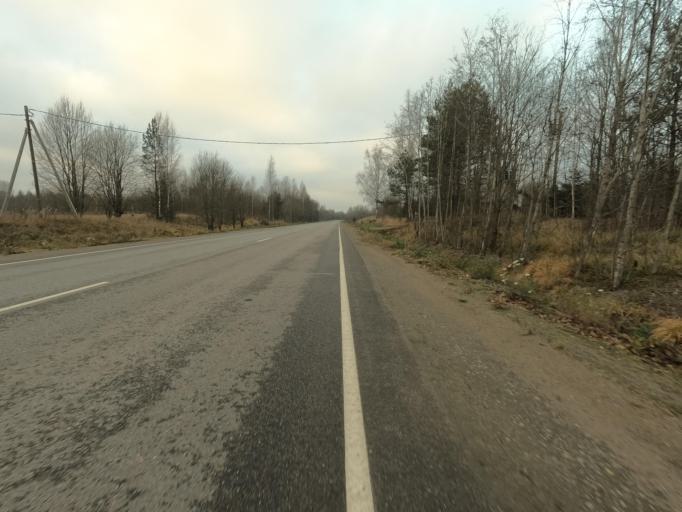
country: RU
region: Leningrad
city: Pavlovo
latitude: 59.8033
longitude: 30.9691
